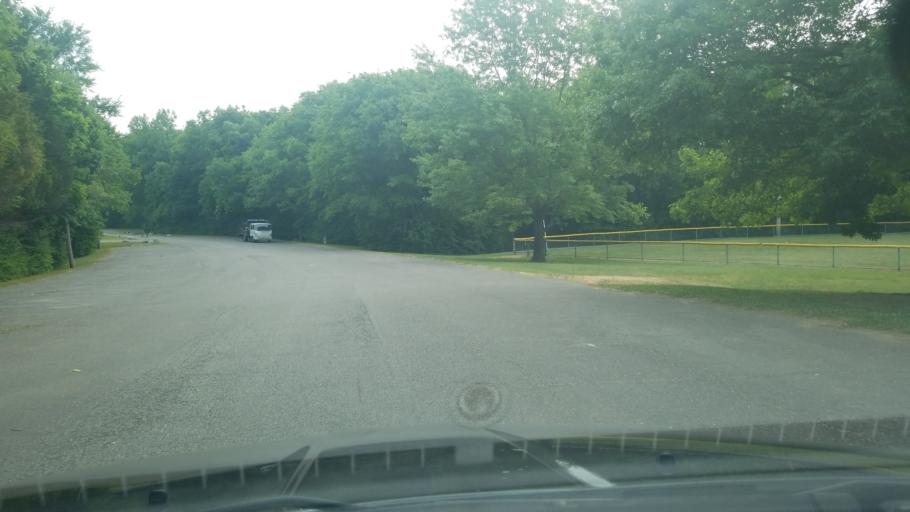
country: US
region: Tennessee
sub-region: Davidson County
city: Goodlettsville
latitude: 36.2704
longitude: -86.7498
